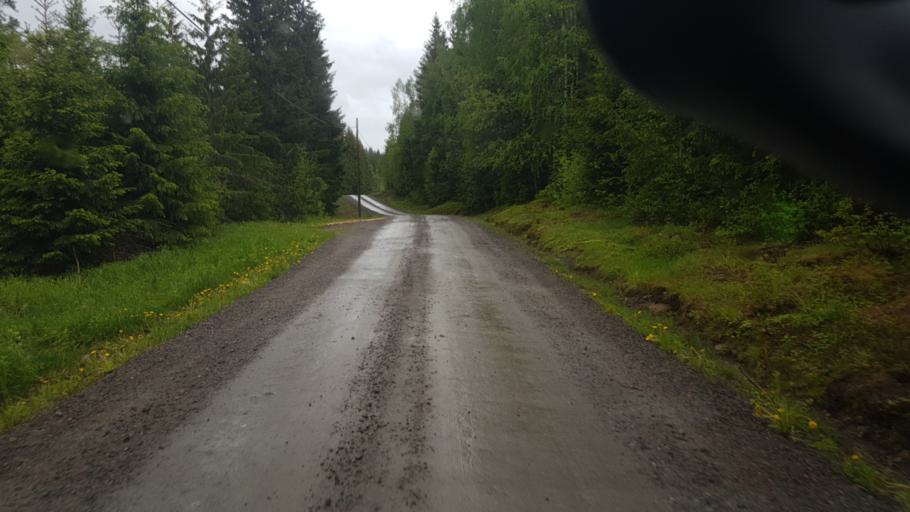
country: SE
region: Vaermland
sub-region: Eda Kommun
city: Charlottenberg
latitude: 59.9202
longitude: 12.3785
